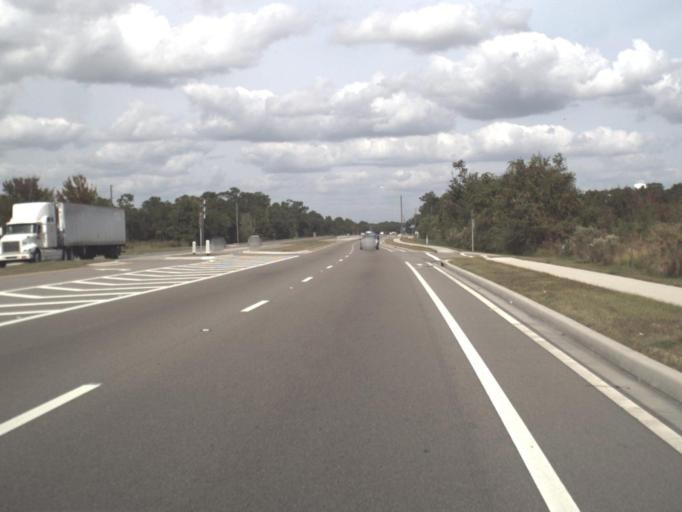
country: US
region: Florida
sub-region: Osceola County
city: Campbell
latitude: 28.2410
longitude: -81.4872
